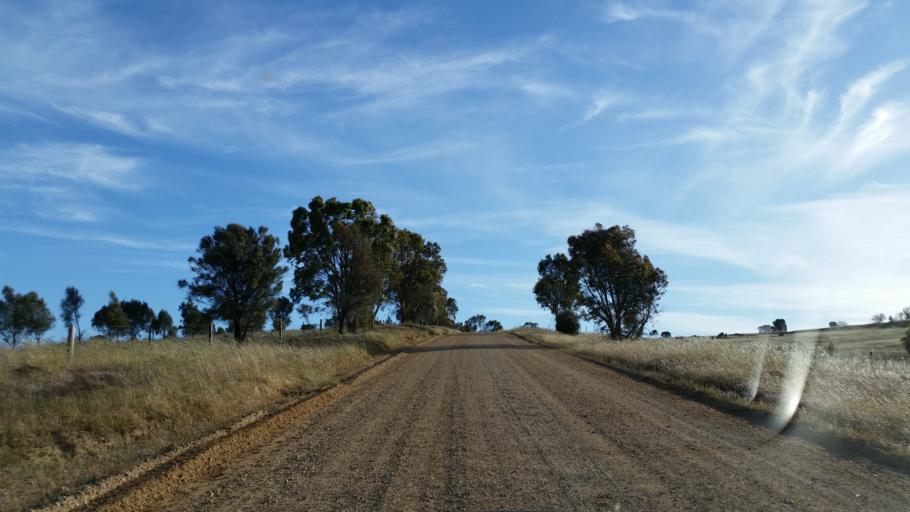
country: AU
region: South Australia
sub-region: Adelaide Hills
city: Birdwood
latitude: -34.7074
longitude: 139.1689
